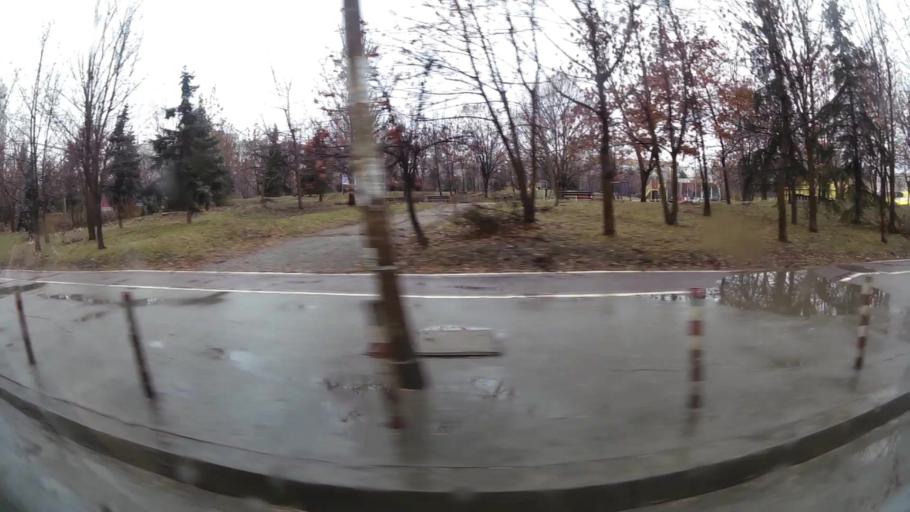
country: BG
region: Sofia-Capital
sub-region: Stolichna Obshtina
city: Sofia
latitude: 42.6418
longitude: 23.3809
